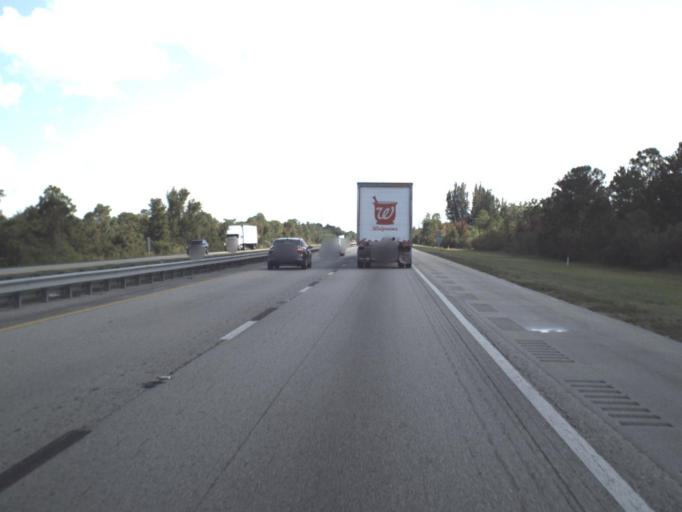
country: US
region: Florida
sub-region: Indian River County
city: Fellsmere
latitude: 27.7363
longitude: -80.9226
